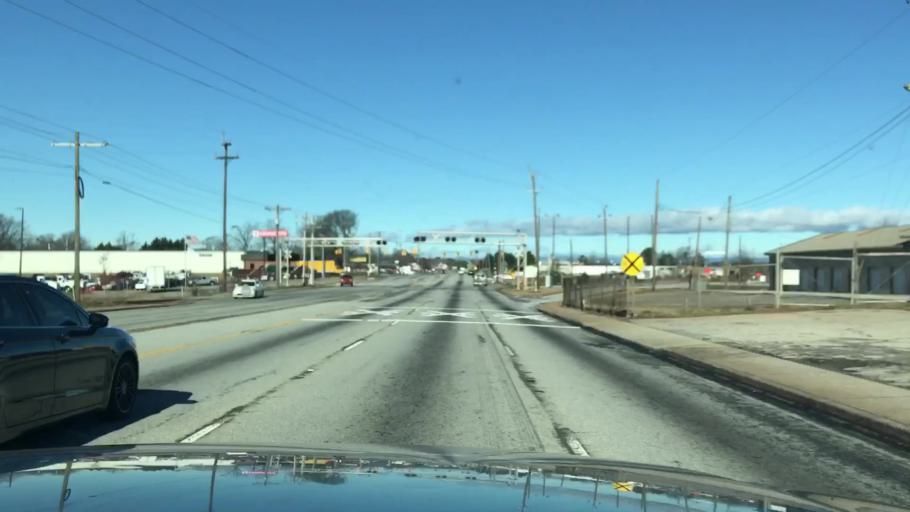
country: US
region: South Carolina
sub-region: Greenville County
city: Gantt
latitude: 34.8048
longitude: -82.4315
